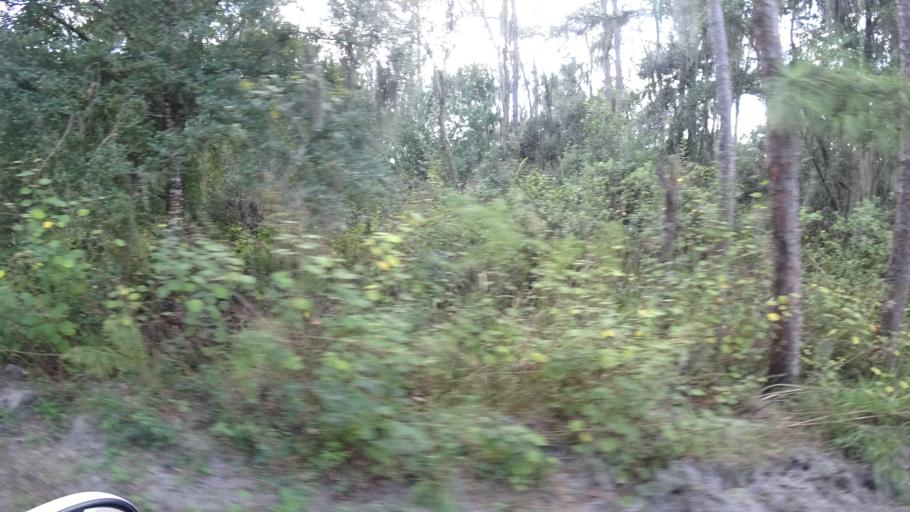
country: US
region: Florida
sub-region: DeSoto County
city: Arcadia
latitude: 27.3516
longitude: -82.1157
